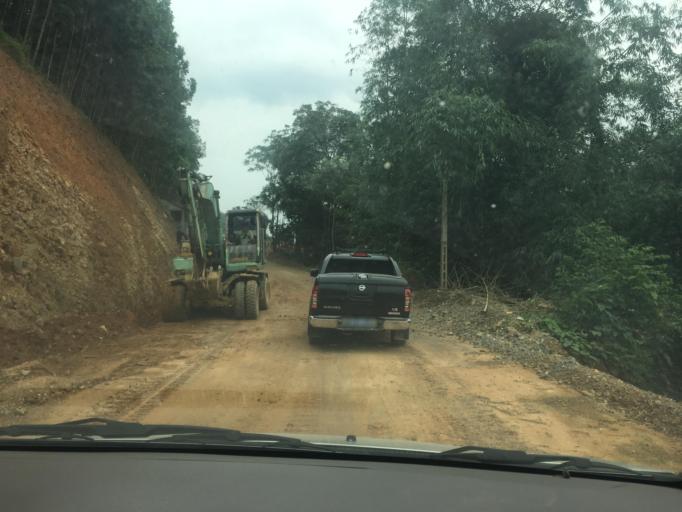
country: VN
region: Lang Son
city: Binh Gia
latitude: 22.1271
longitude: 106.3529
